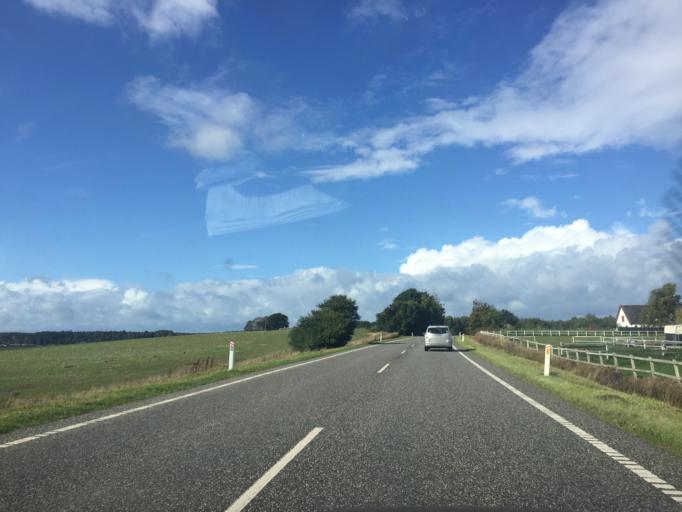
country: DK
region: Capital Region
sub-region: Gribskov Kommune
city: Helsinge
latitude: 56.0398
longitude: 12.1400
